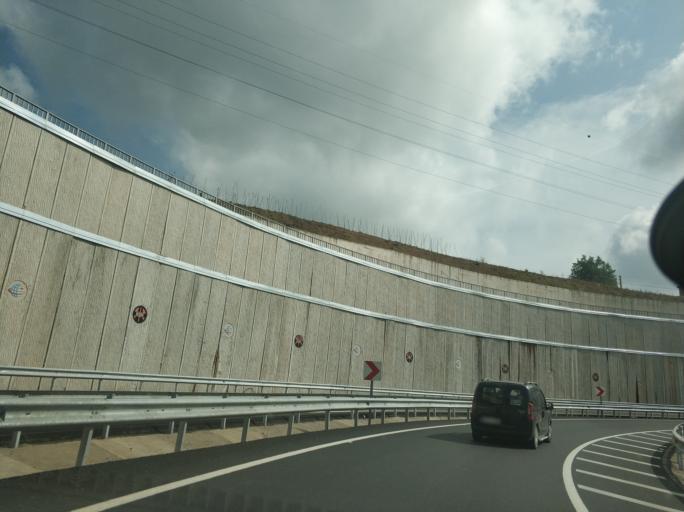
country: TR
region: Ordu
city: Ordu
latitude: 40.9531
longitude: 37.9043
